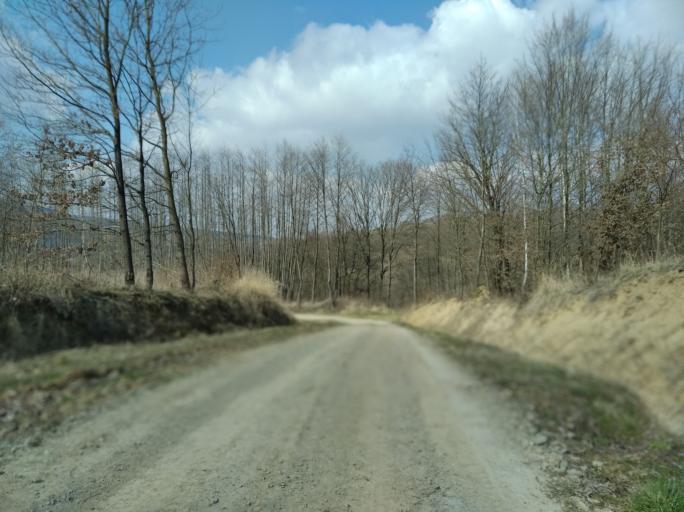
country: PL
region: Subcarpathian Voivodeship
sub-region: Powiat strzyzowski
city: Jawornik
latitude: 49.8212
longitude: 21.8476
